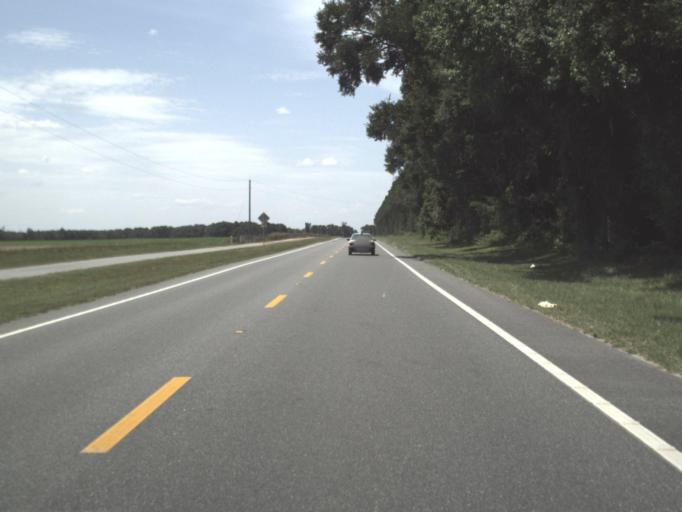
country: US
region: Florida
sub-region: Alachua County
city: High Springs
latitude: 29.9189
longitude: -82.8602
